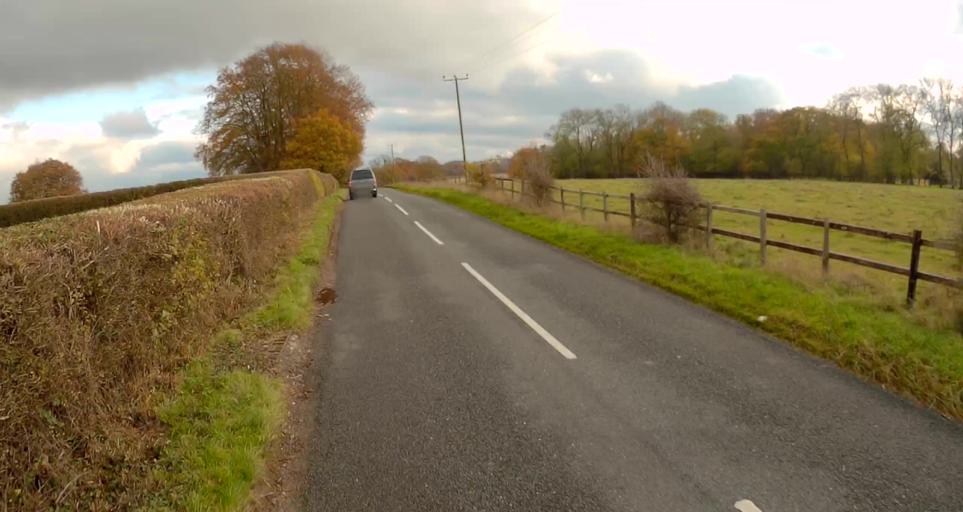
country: GB
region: England
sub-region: Hampshire
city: Old Basing
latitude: 51.2393
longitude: -1.0361
